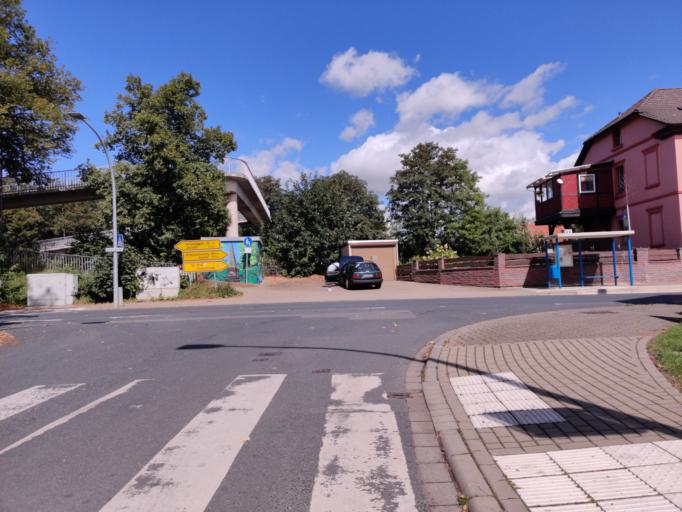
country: DE
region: Lower Saxony
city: Alt Wallmoden
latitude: 52.0371
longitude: 10.3073
